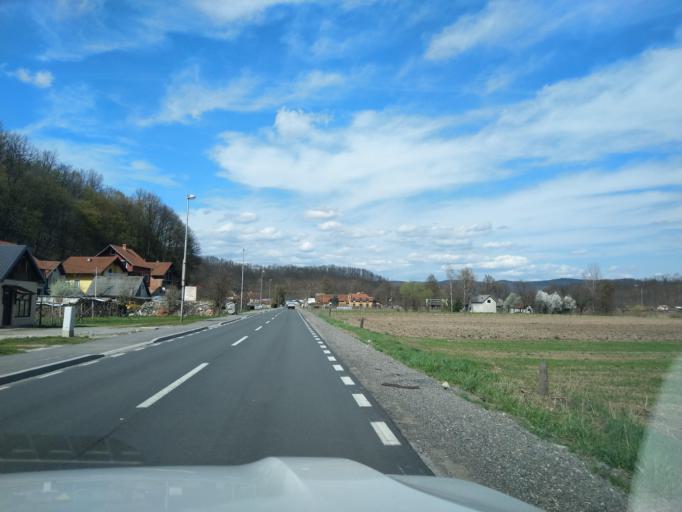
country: RS
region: Central Serbia
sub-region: Zlatiborski Okrug
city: Arilje
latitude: 43.7757
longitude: 20.1018
